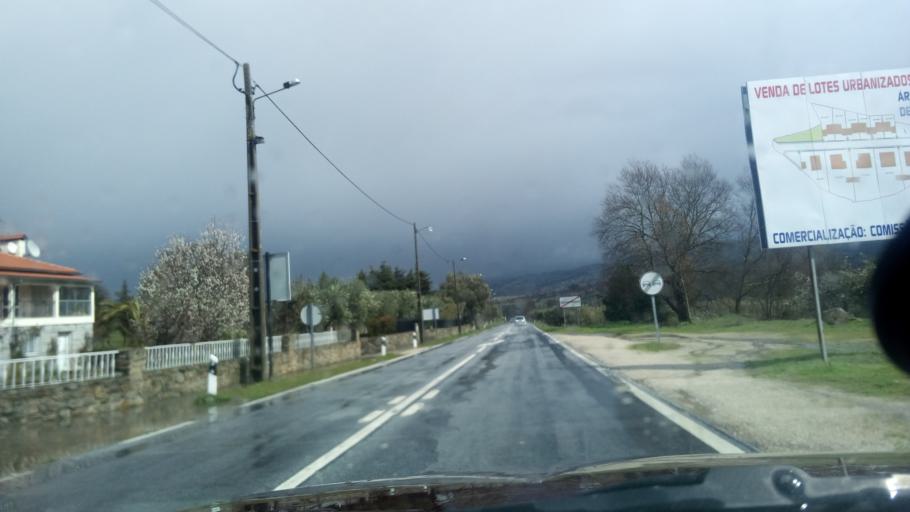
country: PT
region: Guarda
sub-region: Fornos de Algodres
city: Fornos de Algodres
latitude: 40.5605
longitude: -7.4822
